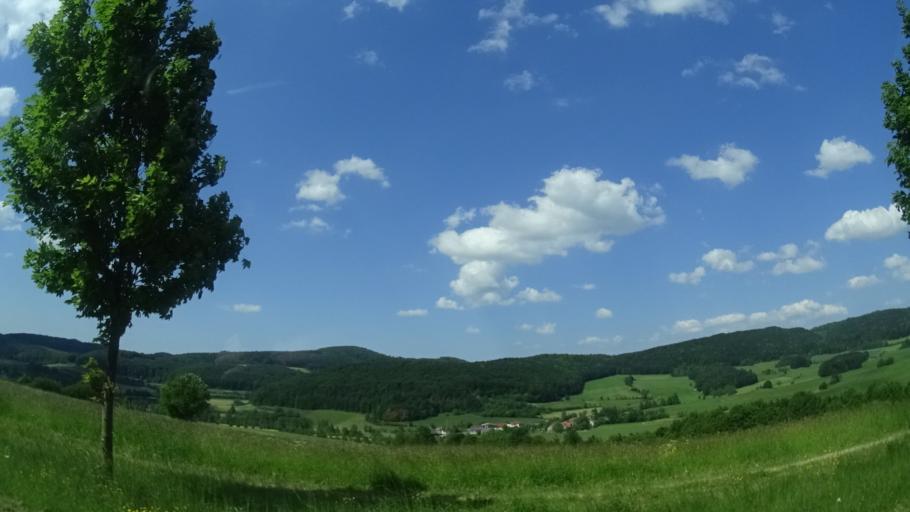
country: DE
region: Hesse
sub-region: Regierungsbezirk Kassel
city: Hofbieber
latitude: 50.6140
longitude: 9.9137
